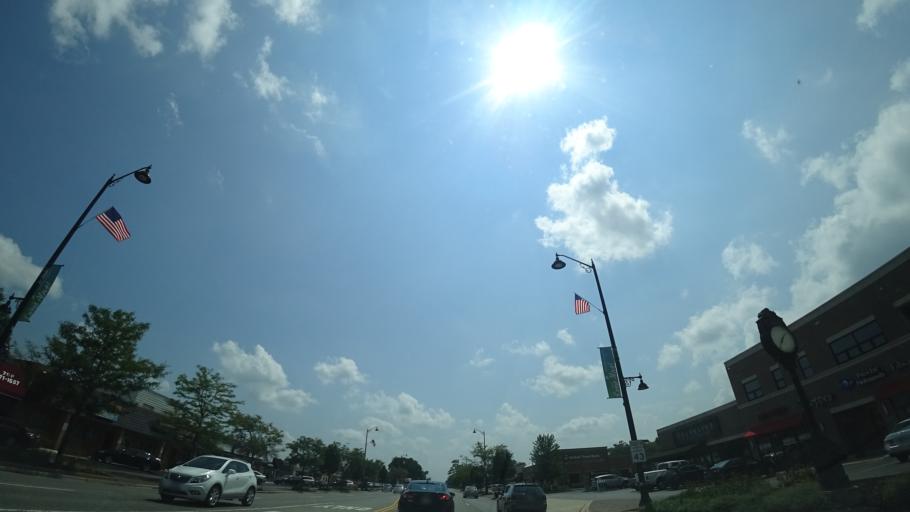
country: US
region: Illinois
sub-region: Cook County
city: Palos Heights
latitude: 41.6679
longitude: -87.7966
